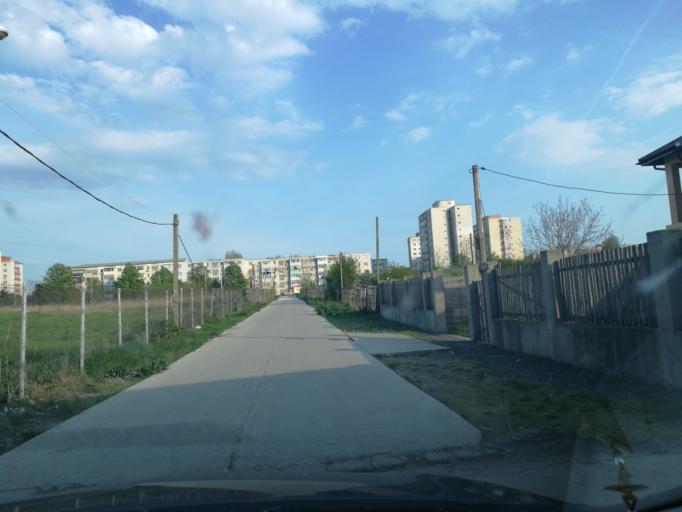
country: RO
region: Constanta
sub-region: Municipiul Constanta
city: Palazu Mare
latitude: 44.2141
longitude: 28.6212
